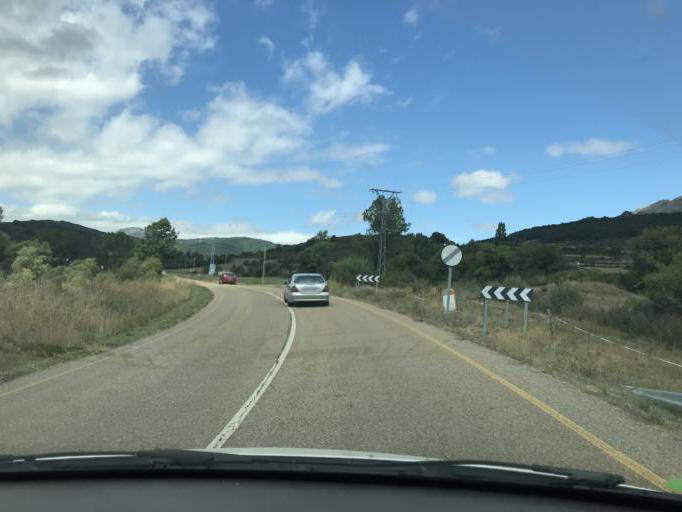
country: ES
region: Castille and Leon
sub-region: Provincia de Palencia
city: Polentinos
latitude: 42.9627
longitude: -4.4872
